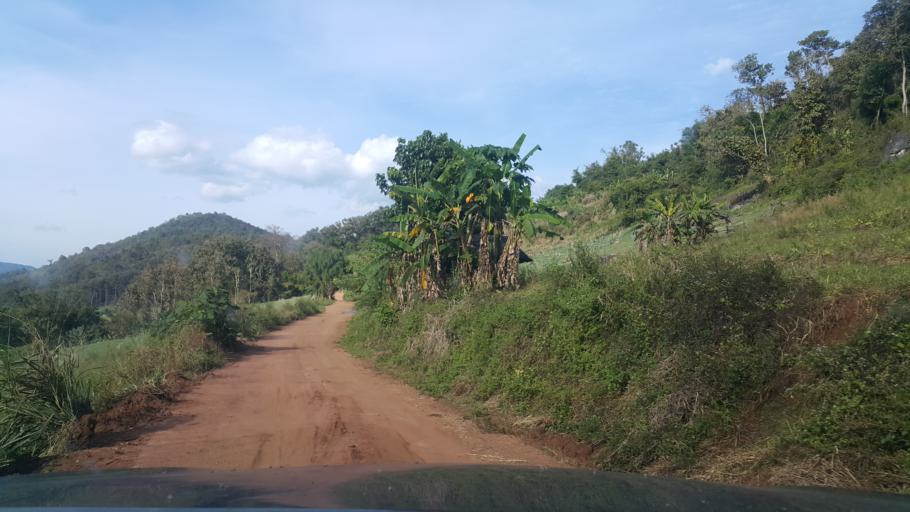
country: TH
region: Chiang Mai
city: Samoeng
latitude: 18.9669
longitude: 98.6801
